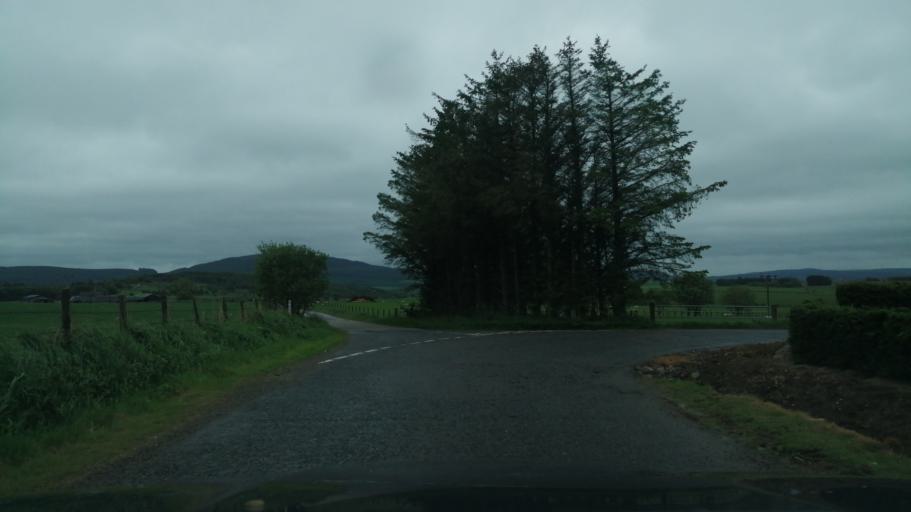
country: GB
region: Scotland
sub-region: Moray
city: Keith
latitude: 57.5761
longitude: -2.8599
